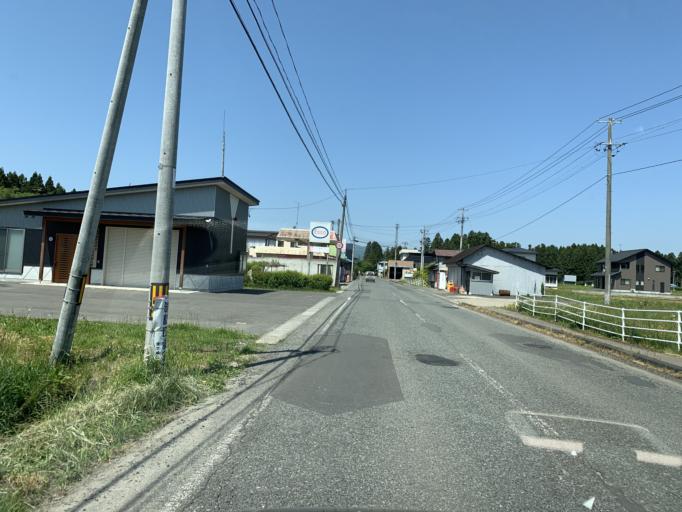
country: JP
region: Iwate
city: Mizusawa
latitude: 39.1955
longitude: 141.0744
